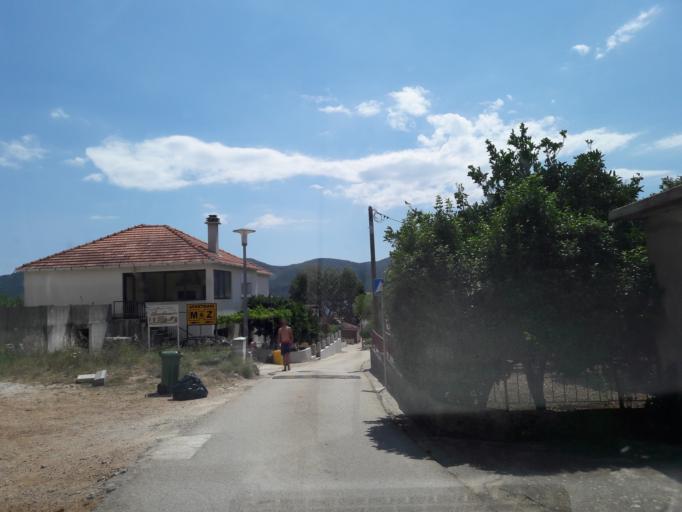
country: HR
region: Dubrovacko-Neretvanska
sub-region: Grad Korcula
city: Zrnovo
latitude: 42.9824
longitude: 17.1035
